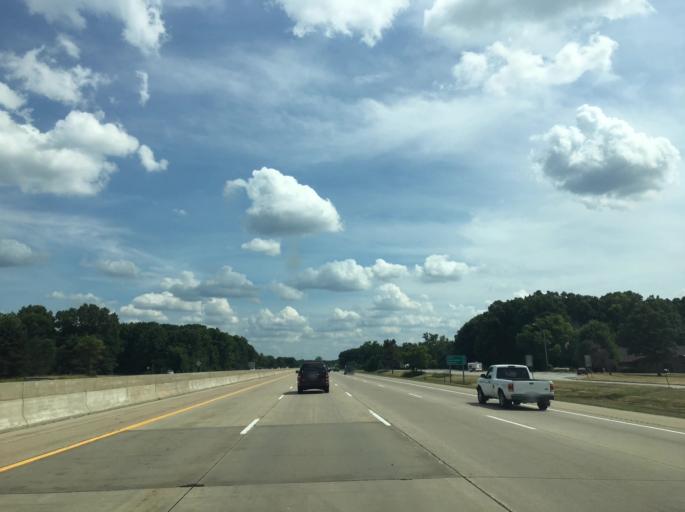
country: US
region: Michigan
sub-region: Genesee County
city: Clio
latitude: 43.1595
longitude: -83.7668
